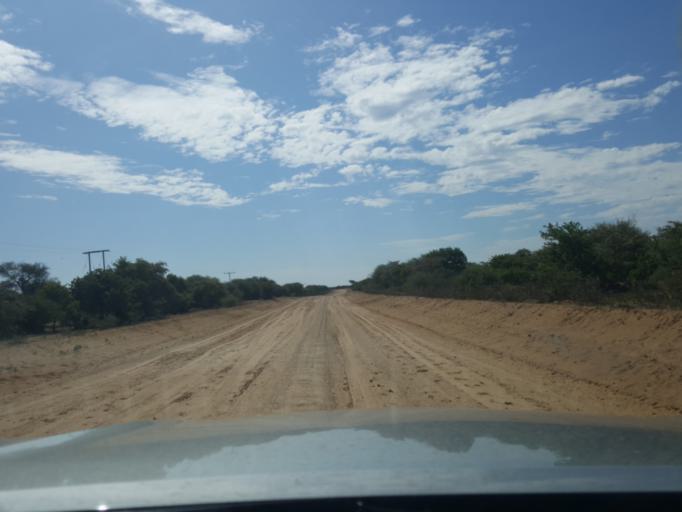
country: BW
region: Kweneng
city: Khudumelapye
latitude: -23.8663
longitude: 24.8915
